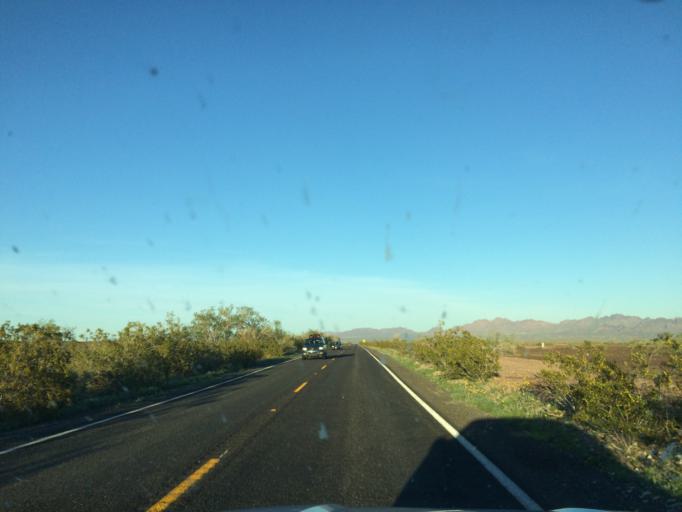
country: US
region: California
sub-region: Riverside County
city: Mesa Verde
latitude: 33.2859
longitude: -114.7691
